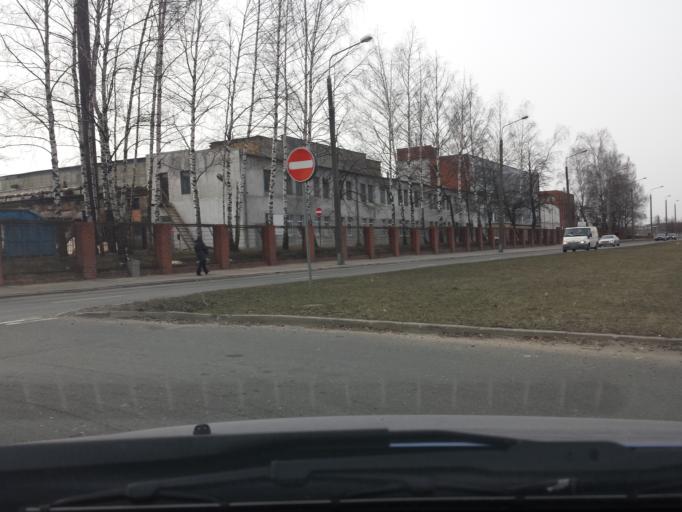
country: LV
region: Riga
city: Riga
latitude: 56.9184
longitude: 24.1147
